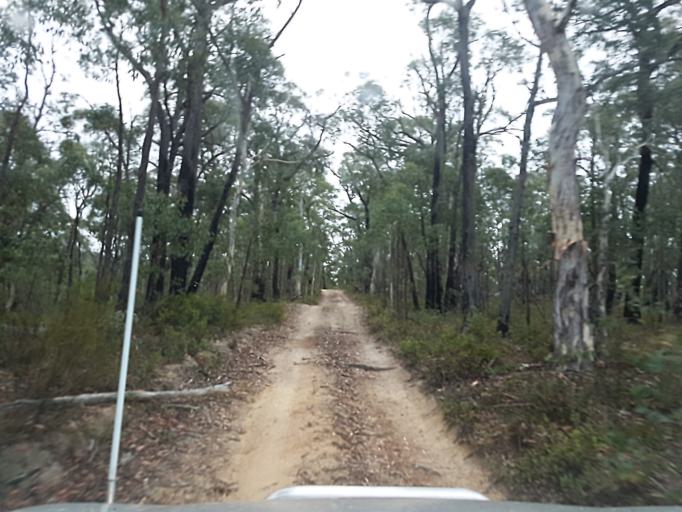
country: AU
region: New South Wales
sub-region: Snowy River
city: Jindabyne
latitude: -36.8509
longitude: 148.2269
